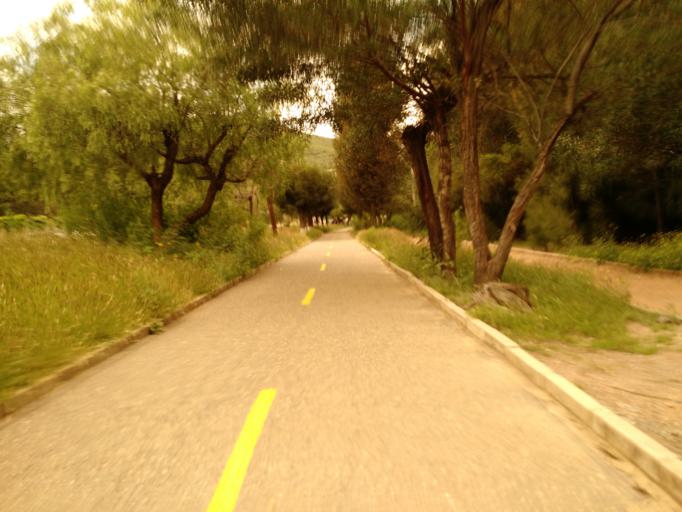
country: BO
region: Cochabamba
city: Cochabamba
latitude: -17.4041
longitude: -66.1304
